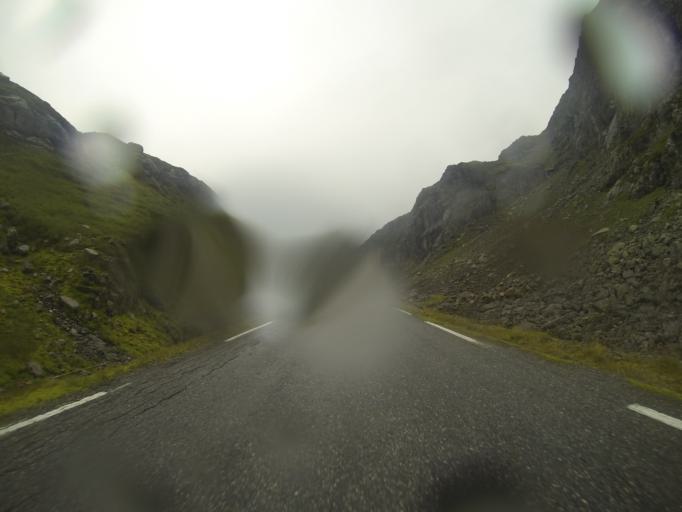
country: NO
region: Hordaland
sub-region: Odda
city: Odda
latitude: 59.7701
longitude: 6.7405
